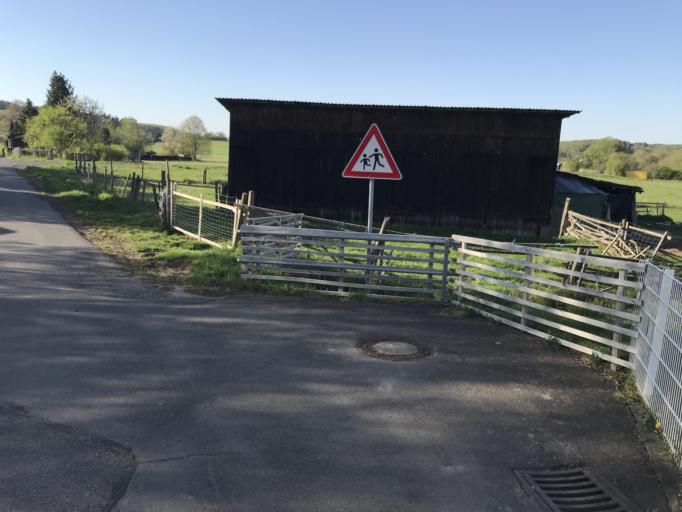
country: DE
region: Hesse
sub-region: Regierungsbezirk Giessen
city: Grossen Buseck
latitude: 50.5847
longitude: 8.8032
